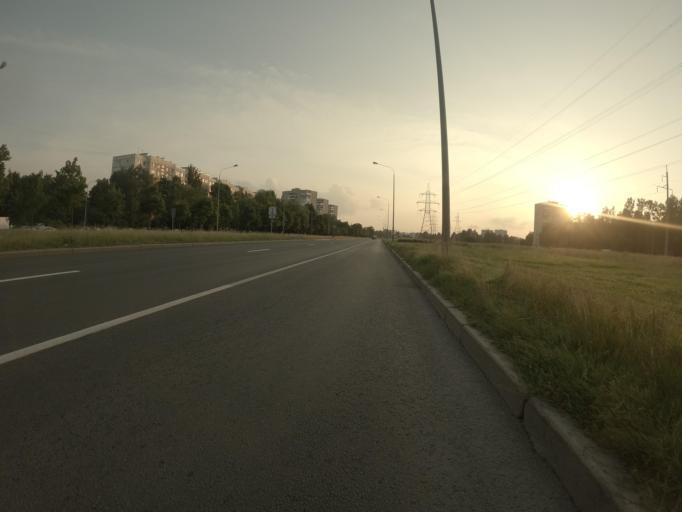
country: RU
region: Leningrad
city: Kalininskiy
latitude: 59.9747
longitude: 30.4236
